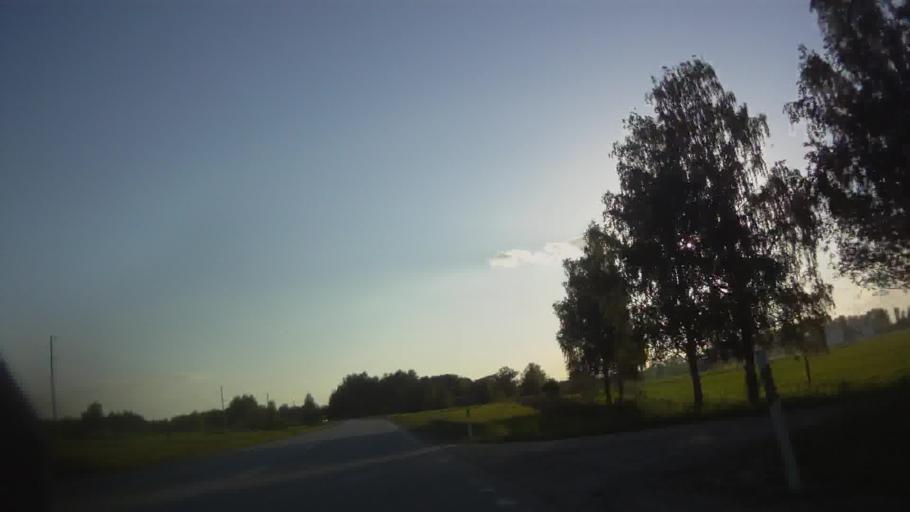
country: LV
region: Livani
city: Livani
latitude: 56.5338
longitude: 26.2508
